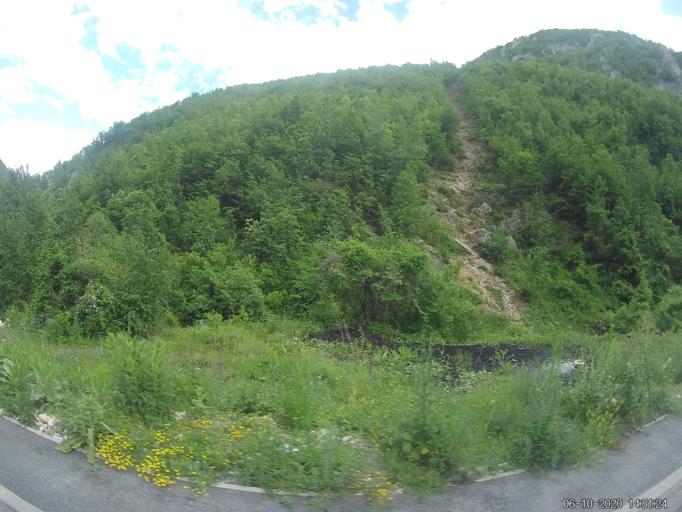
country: XK
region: Prizren
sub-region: Komuna e Therandes
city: Budakovo
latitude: 42.3991
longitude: 20.9750
